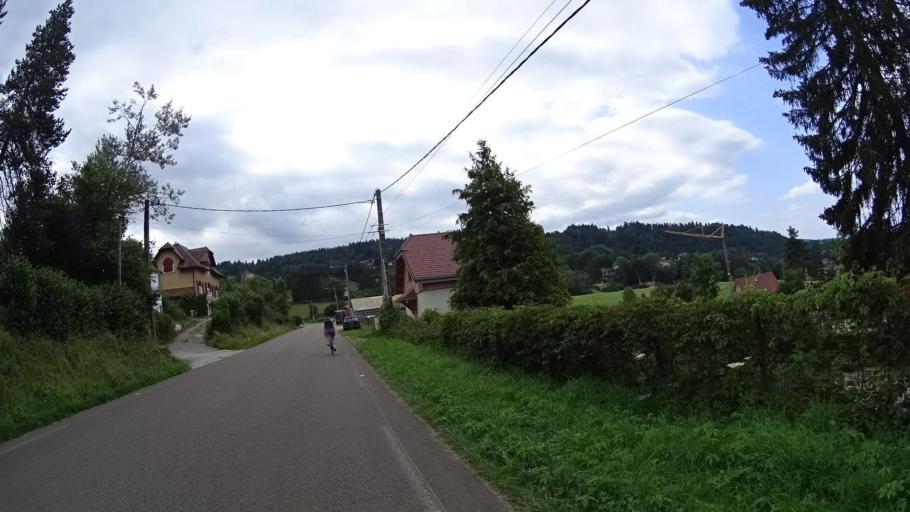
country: FR
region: Franche-Comte
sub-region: Departement du Doubs
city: Les Fourgs
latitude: 46.8375
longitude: 6.3427
